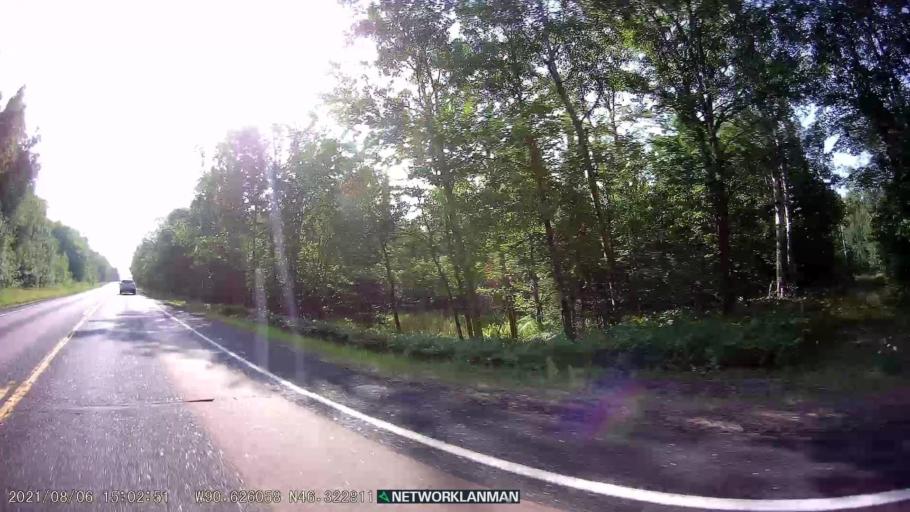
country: US
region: Wisconsin
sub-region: Ashland County
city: Ashland
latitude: 46.3227
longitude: -90.6264
